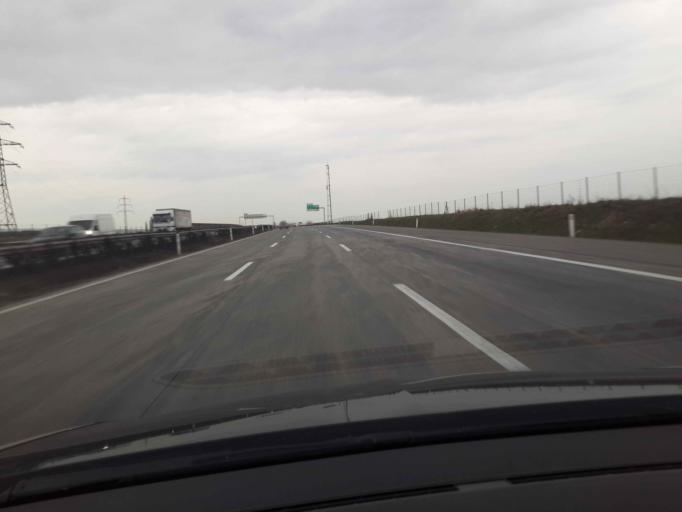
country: AT
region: Lower Austria
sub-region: Sankt Polten Stadt
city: Sankt Poelten
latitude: 48.1779
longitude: 15.5953
